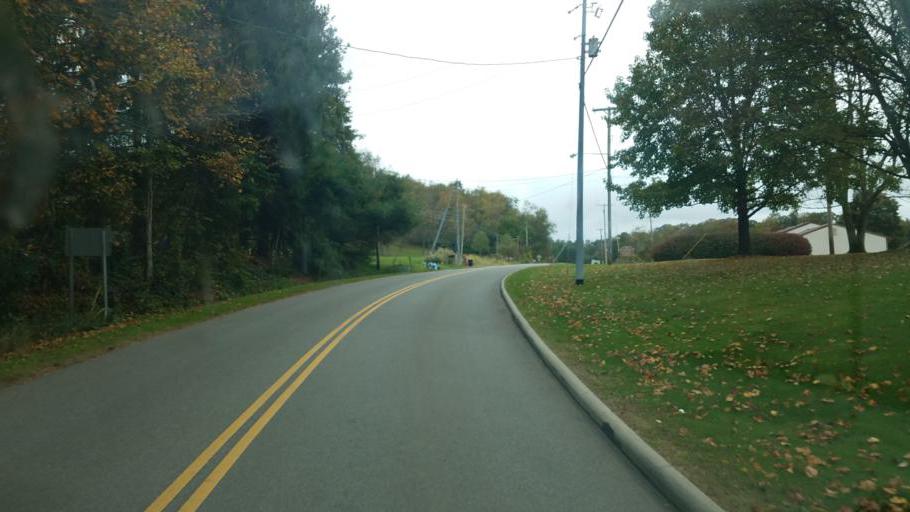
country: US
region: Ohio
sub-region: Ashland County
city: Loudonville
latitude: 40.6263
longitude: -82.2436
